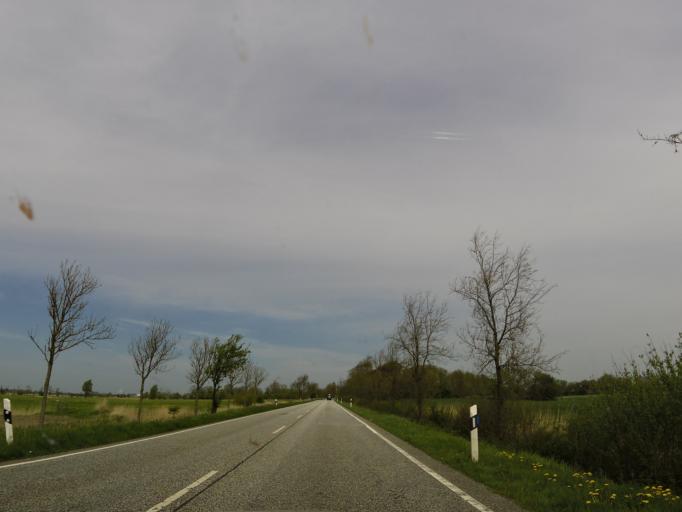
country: DE
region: Schleswig-Holstein
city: Oldenswort
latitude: 54.3491
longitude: 8.9709
